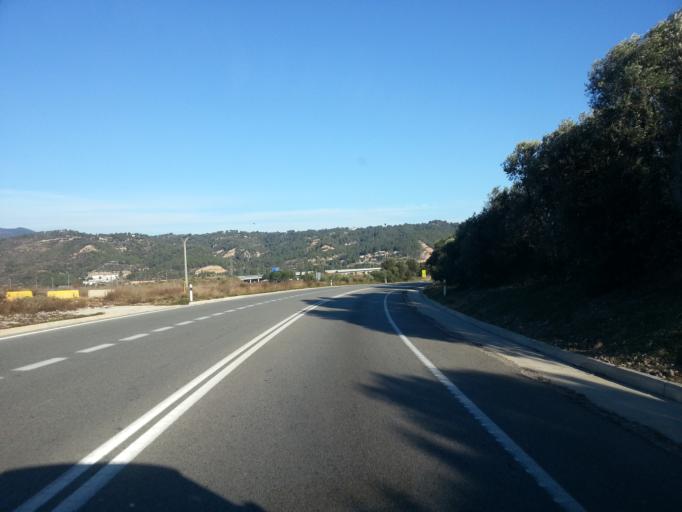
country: ES
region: Catalonia
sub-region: Provincia de Barcelona
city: Abrera
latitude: 41.5239
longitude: 1.9001
